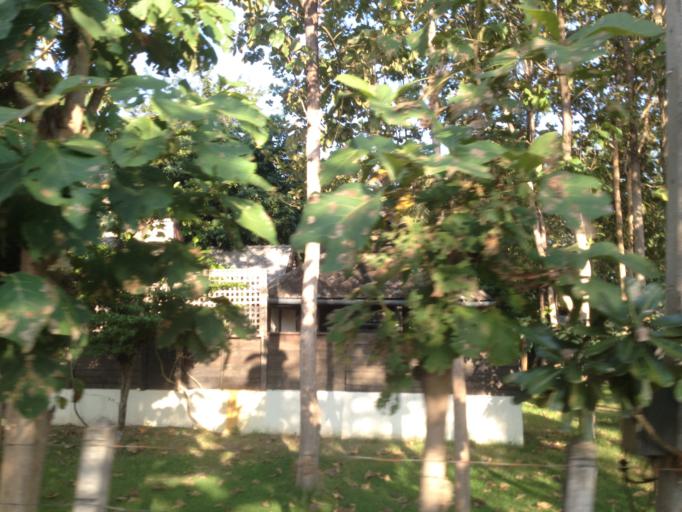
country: TH
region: Chiang Mai
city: Hang Dong
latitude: 18.7181
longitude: 98.9051
